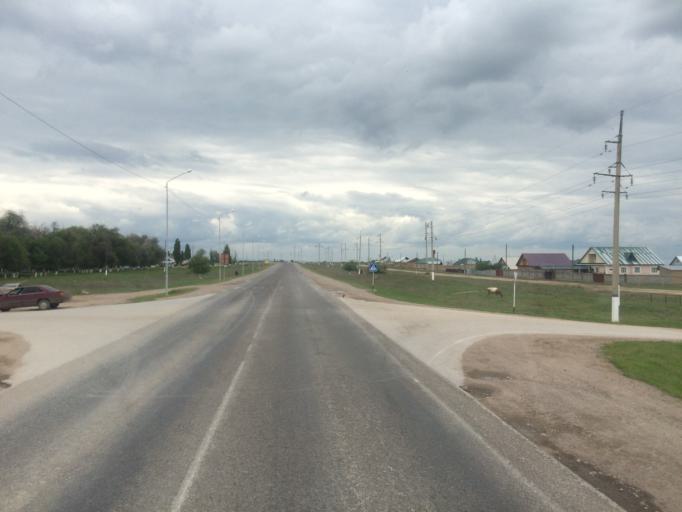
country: KG
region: Chuy
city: Sokuluk
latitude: 43.2483
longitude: 74.2945
